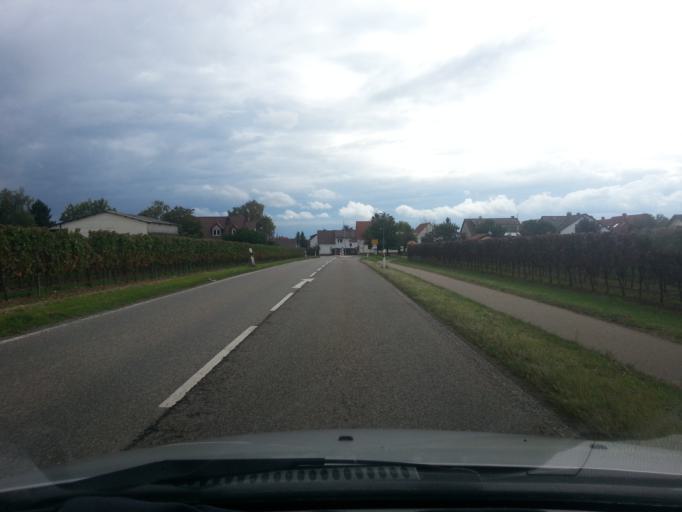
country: DE
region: Rheinland-Pfalz
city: Erpolzheim
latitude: 49.4917
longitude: 8.2238
